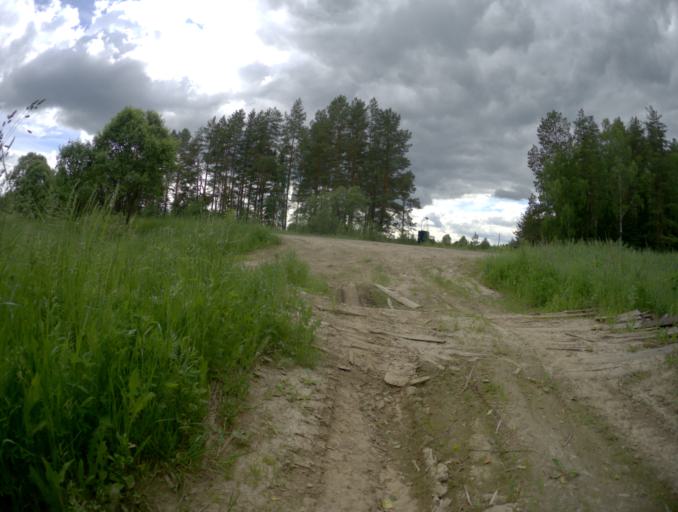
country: RU
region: Ivanovo
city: Kolobovo
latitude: 56.6453
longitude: 41.4159
